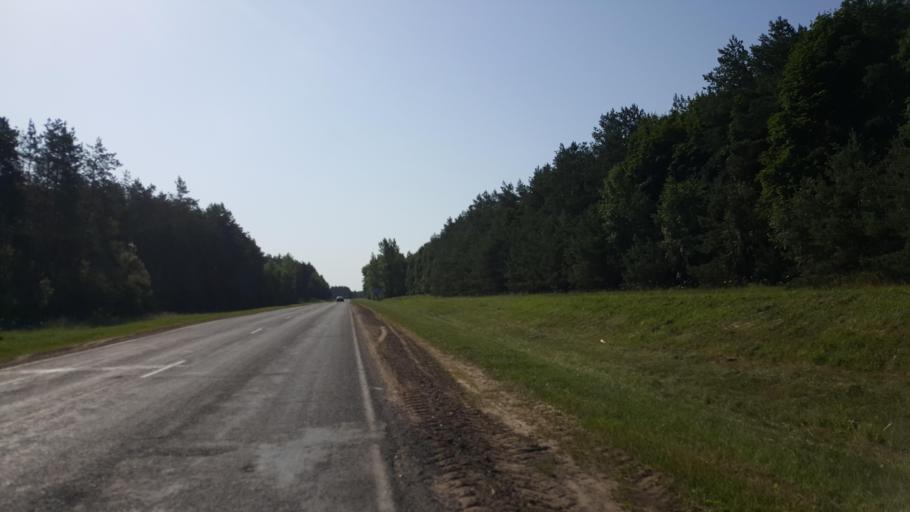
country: BY
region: Brest
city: Kamyanyets
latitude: 52.3901
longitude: 23.8406
